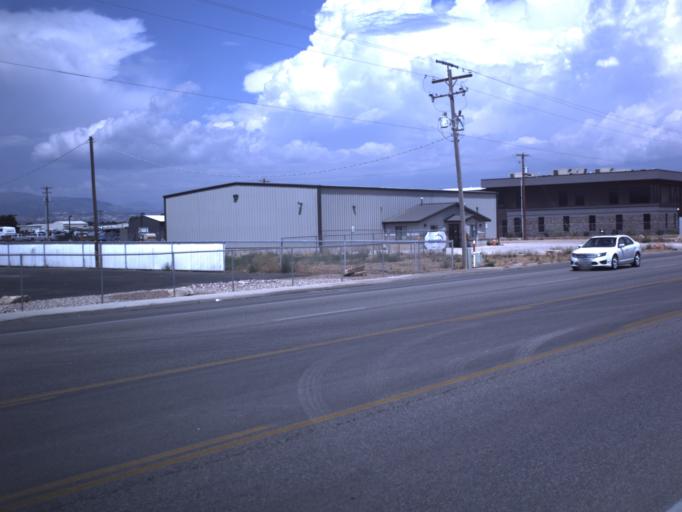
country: US
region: Utah
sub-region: Uintah County
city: Naples
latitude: 40.4423
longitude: -109.4996
